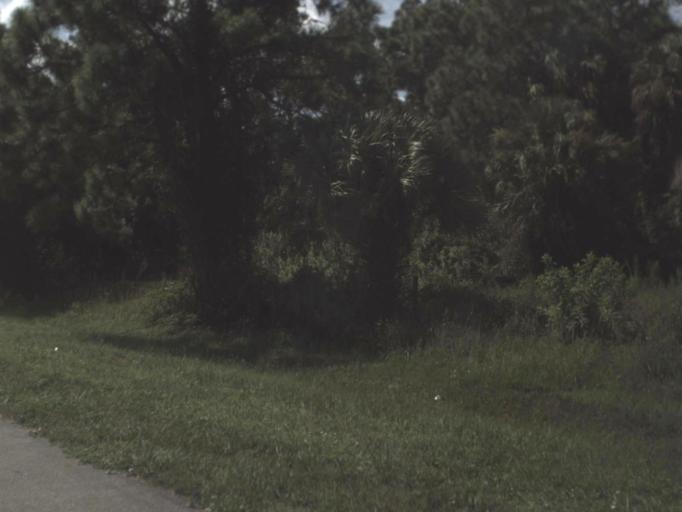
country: US
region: Florida
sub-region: Hendry County
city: LaBelle
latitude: 26.7365
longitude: -81.4378
